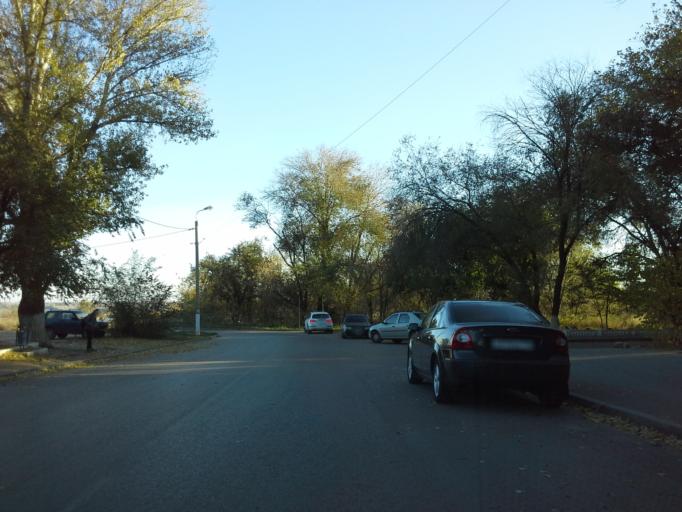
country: RU
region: Volgograd
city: Vodstroy
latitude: 48.8164
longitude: 44.6370
